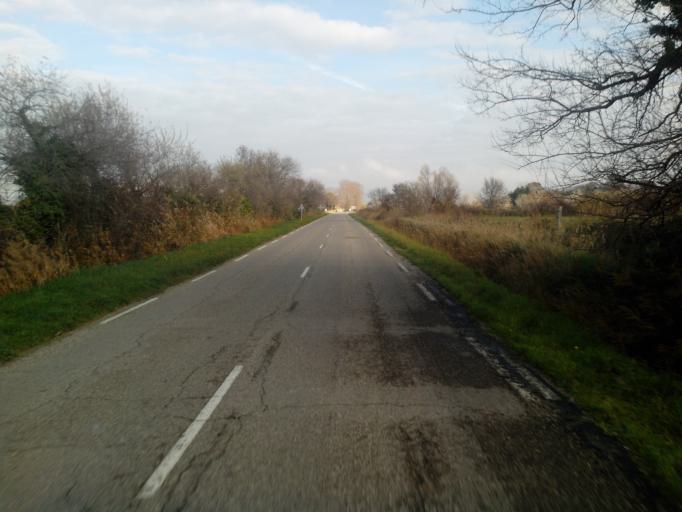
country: FR
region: Provence-Alpes-Cote d'Azur
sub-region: Departement des Bouches-du-Rhone
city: Arles
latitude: 43.5727
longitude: 4.6184
